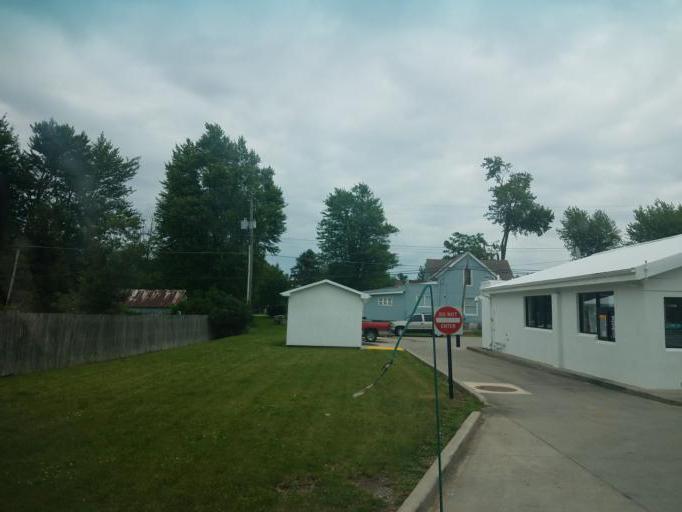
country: US
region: Ohio
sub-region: Hardin County
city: Ada
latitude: 40.7770
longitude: -83.8231
